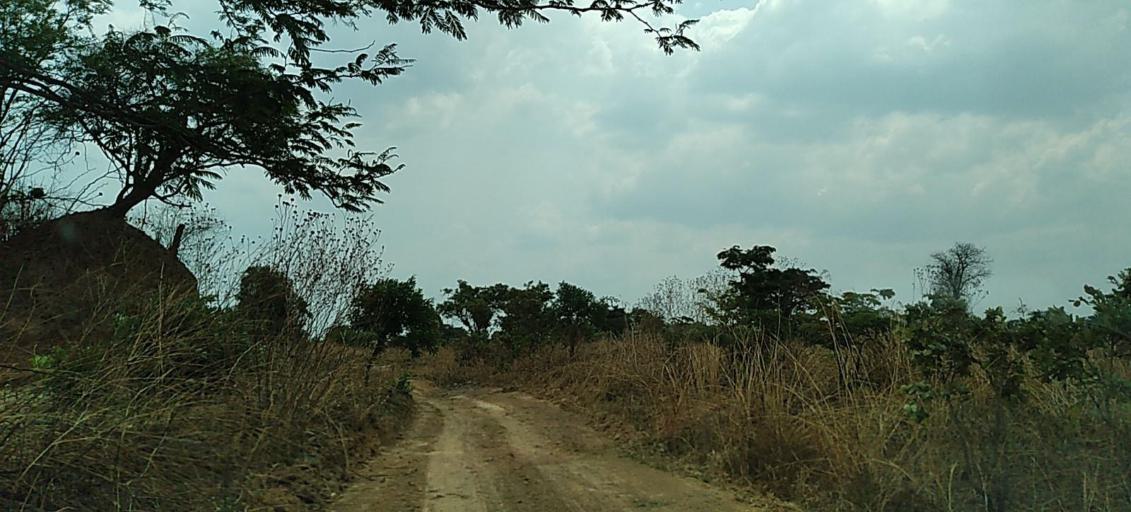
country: ZM
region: Copperbelt
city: Chililabombwe
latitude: -12.3520
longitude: 27.7976
